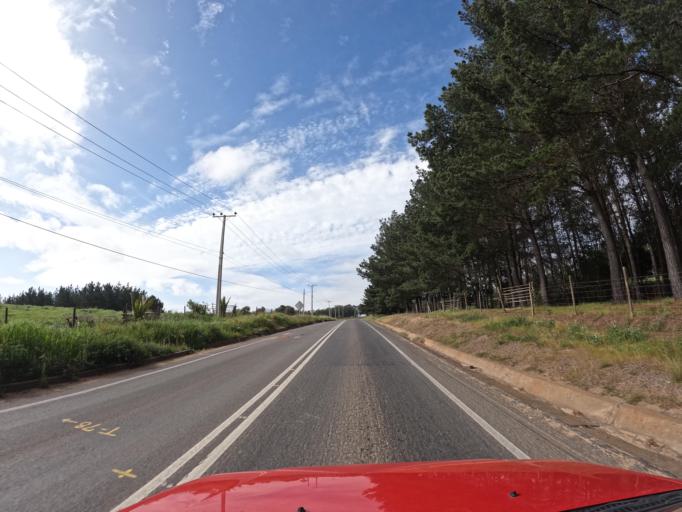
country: CL
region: O'Higgins
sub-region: Provincia de Colchagua
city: Santa Cruz
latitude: -34.3571
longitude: -71.9439
